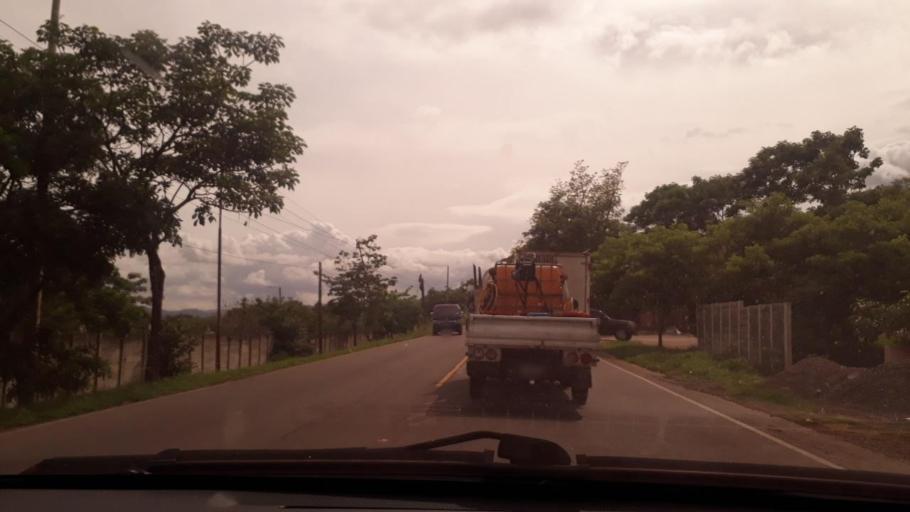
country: GT
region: Jutiapa
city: Jutiapa
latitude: 14.3009
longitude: -89.8800
